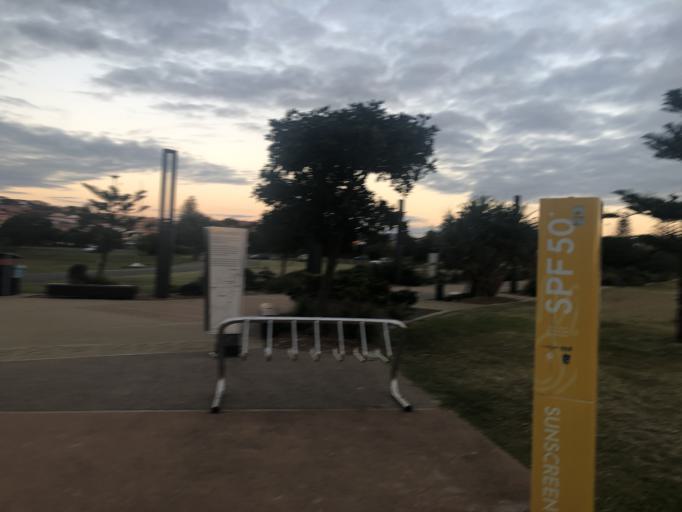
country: AU
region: New South Wales
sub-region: Coffs Harbour
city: Coffs Harbour
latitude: -30.3039
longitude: 153.1404
